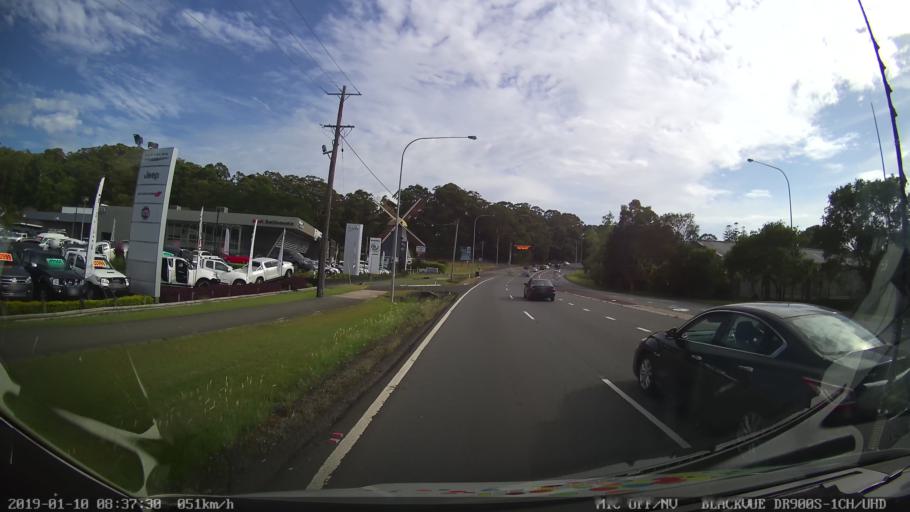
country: AU
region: New South Wales
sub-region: Coffs Harbour
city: Coffs Harbour
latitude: -30.3055
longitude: 153.1018
